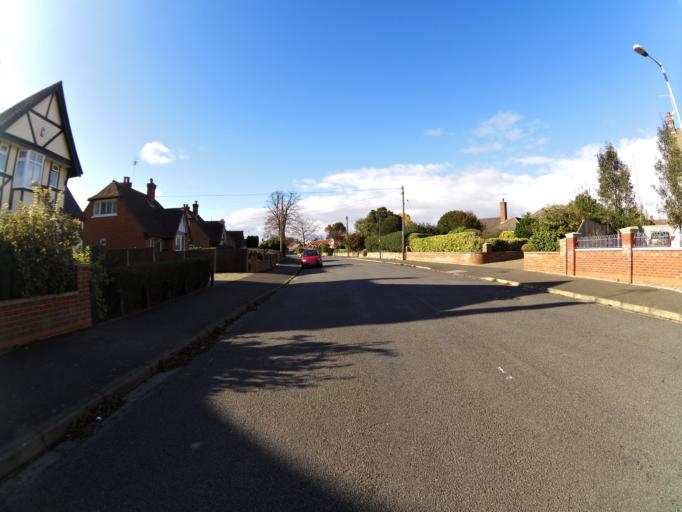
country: GB
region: England
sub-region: Suffolk
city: Felixstowe
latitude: 51.9668
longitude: 1.3576
